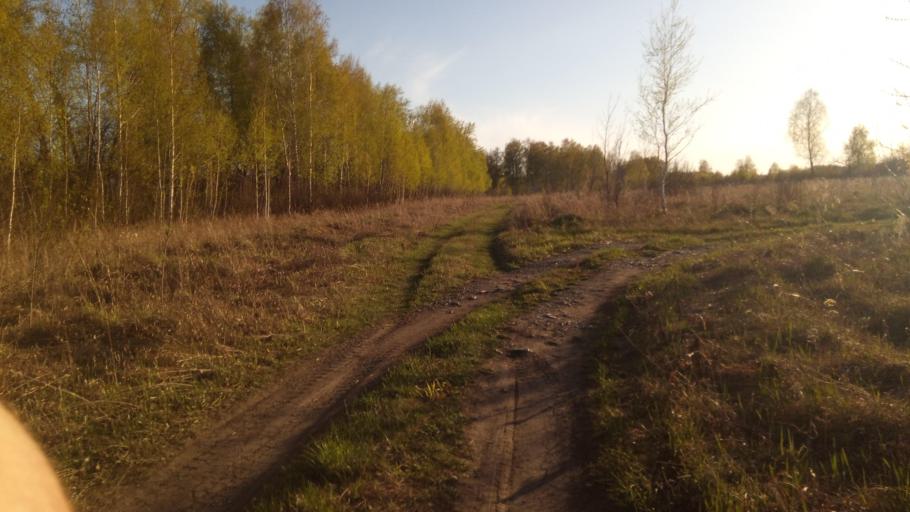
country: RU
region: Chelyabinsk
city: Timiryazevskiy
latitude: 54.9885
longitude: 60.8543
